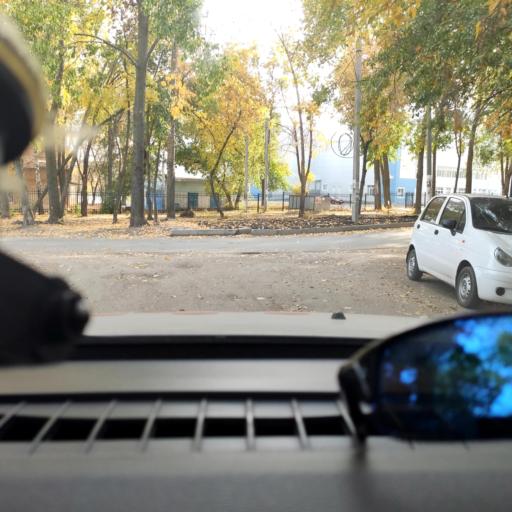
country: RU
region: Samara
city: Samara
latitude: 53.2185
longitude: 50.2125
